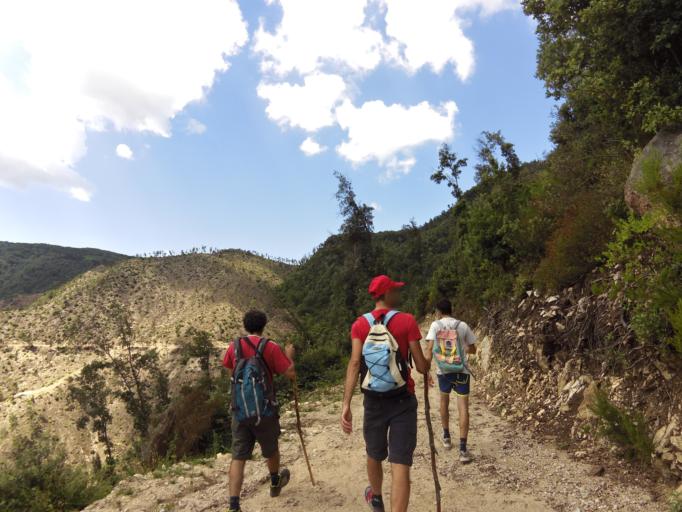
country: IT
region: Calabria
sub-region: Provincia di Reggio Calabria
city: Bivongi
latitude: 38.5059
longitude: 16.3970
